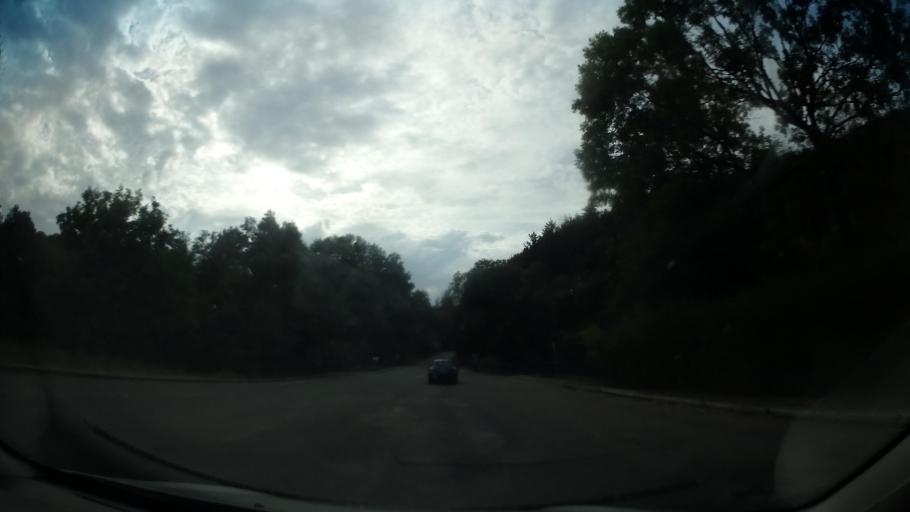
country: CZ
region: Pardubicky
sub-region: Okres Chrudim
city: Sec
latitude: 49.8422
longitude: 15.6791
